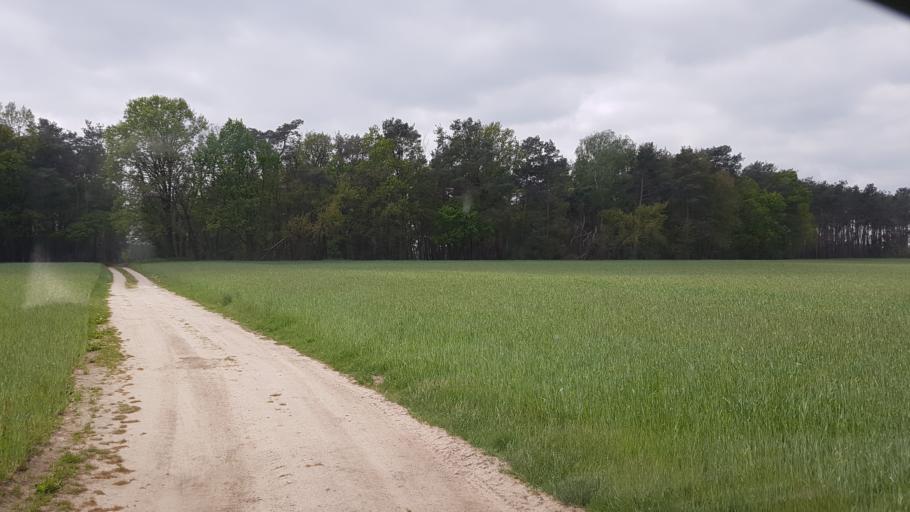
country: DE
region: Brandenburg
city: Schonewalde
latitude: 51.6682
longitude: 13.6184
